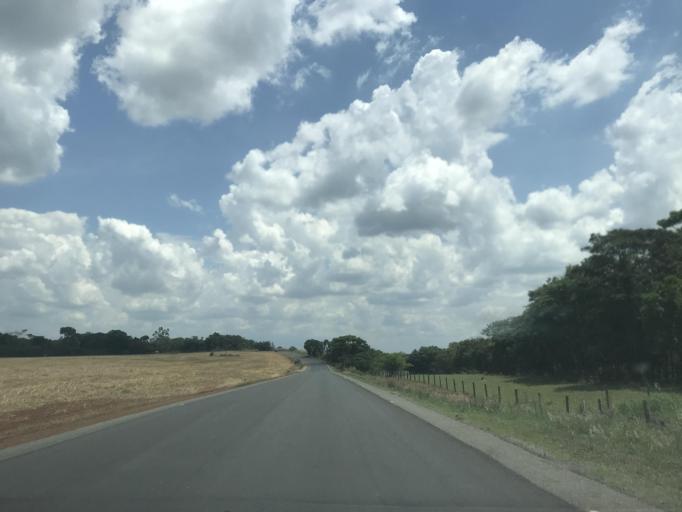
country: BR
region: Goias
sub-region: Piracanjuba
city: Piracanjuba
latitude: -17.3239
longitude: -48.8009
